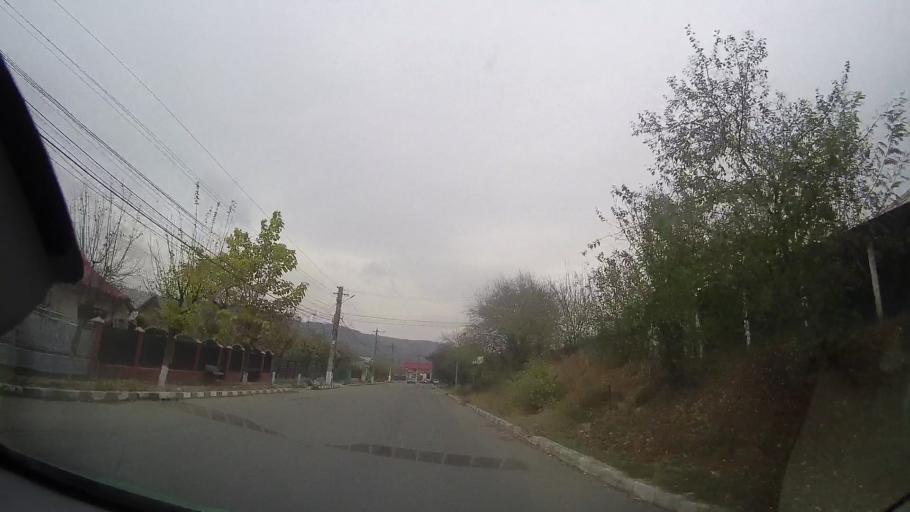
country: RO
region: Prahova
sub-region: Oras Urlati
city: Urlati
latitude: 44.9974
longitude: 26.2293
